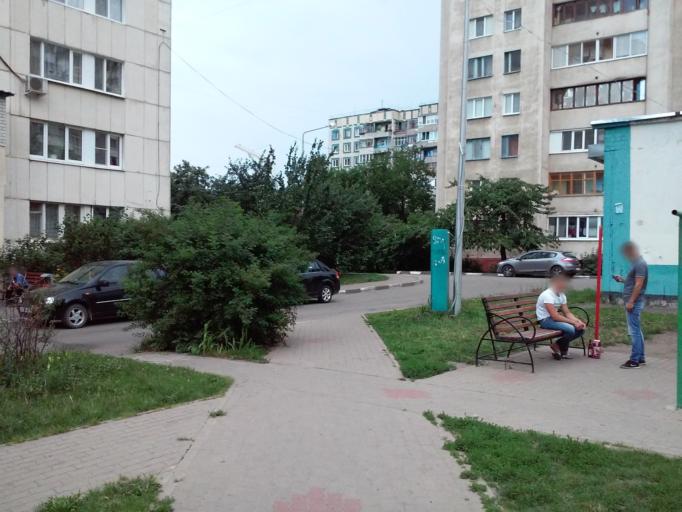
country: RU
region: Belgorod
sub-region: Belgorodskiy Rayon
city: Belgorod
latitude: 50.5722
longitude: 36.5819
